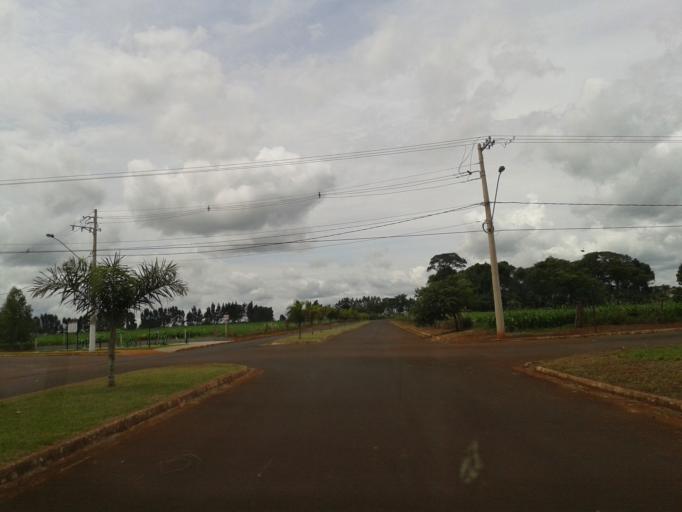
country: BR
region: Minas Gerais
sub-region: Centralina
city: Centralina
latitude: -18.5789
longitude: -49.1995
